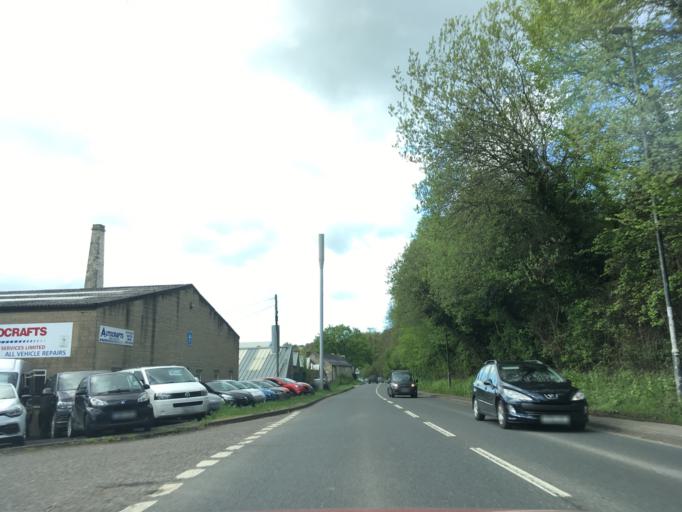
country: GB
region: England
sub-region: Gloucestershire
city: Stroud
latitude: 51.7319
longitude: -2.2041
